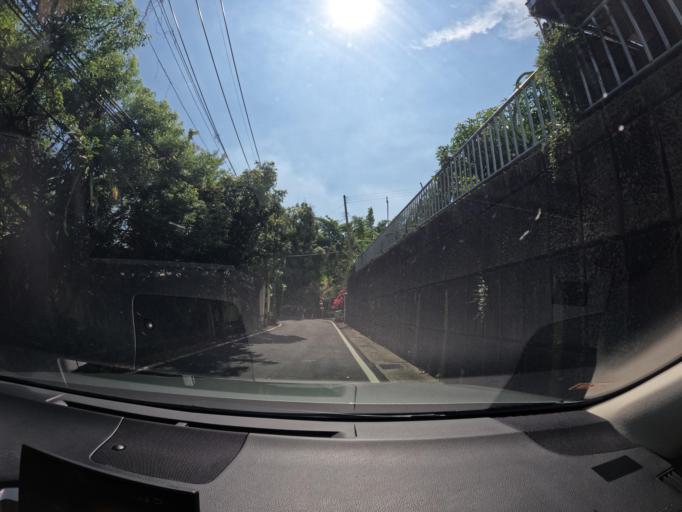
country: TW
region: Taiwan
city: Fengyuan
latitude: 24.3128
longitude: 120.7529
